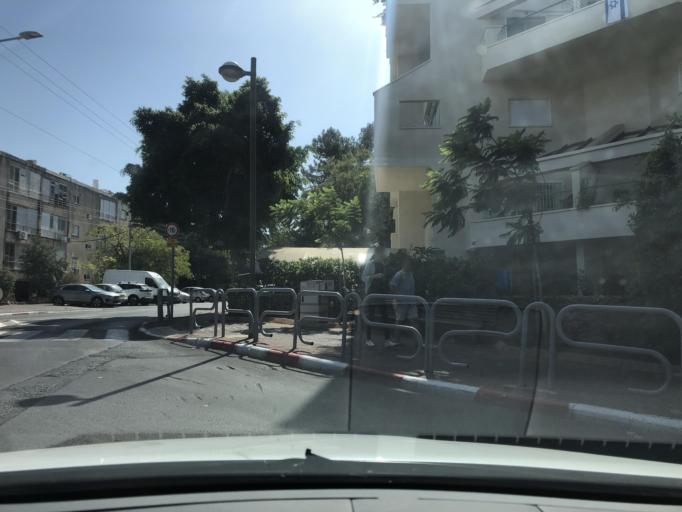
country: IL
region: Central District
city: Kfar Saba
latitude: 32.1756
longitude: 34.8969
